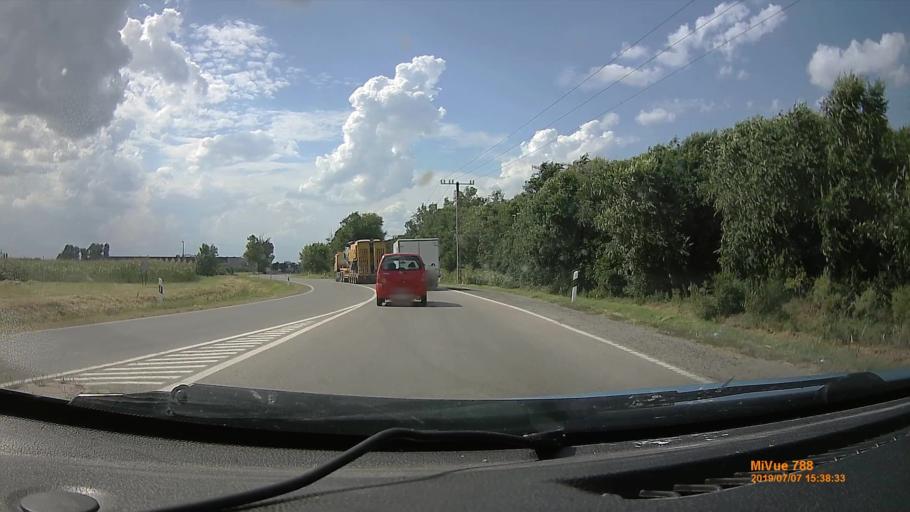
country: HU
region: Jasz-Nagykun-Szolnok
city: Jaszbereny
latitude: 47.4898
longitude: 19.9420
